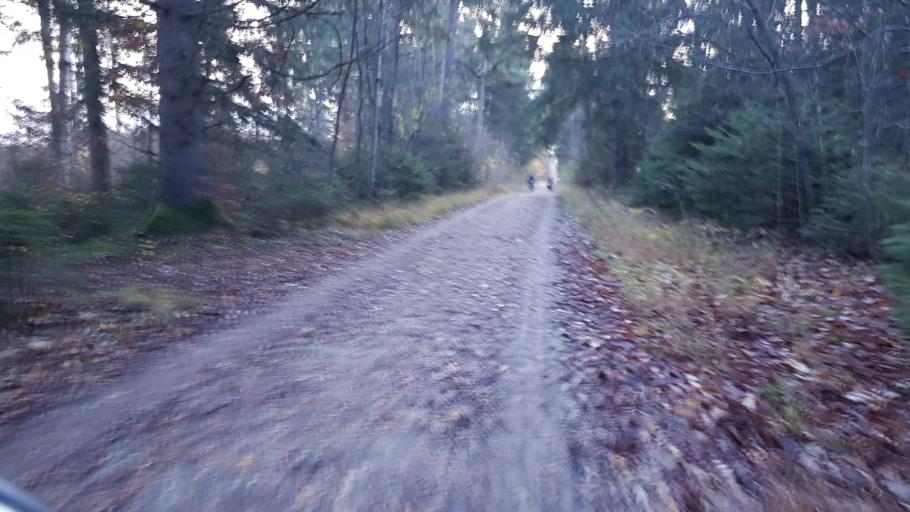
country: DE
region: Bavaria
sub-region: Upper Bavaria
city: Unterhaching
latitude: 48.0824
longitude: 11.5865
